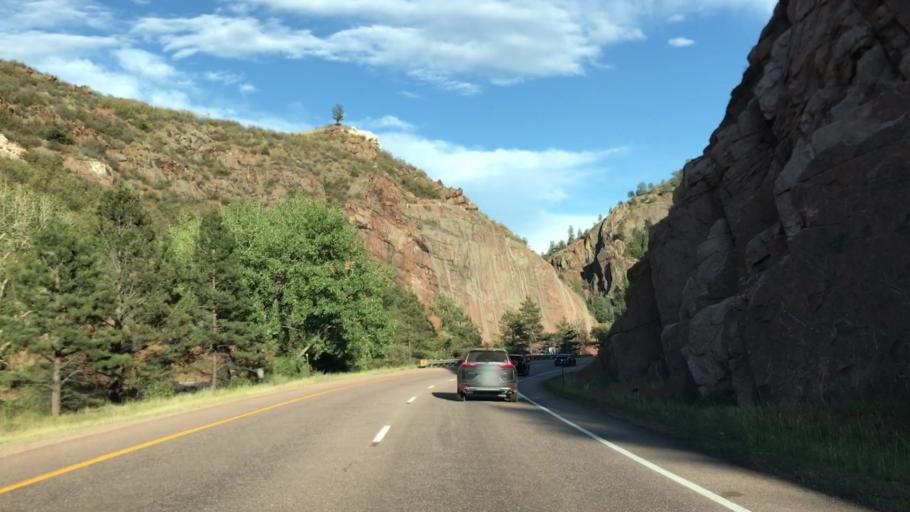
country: US
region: Colorado
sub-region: El Paso County
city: Manitou Springs
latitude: 38.8800
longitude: -104.9476
